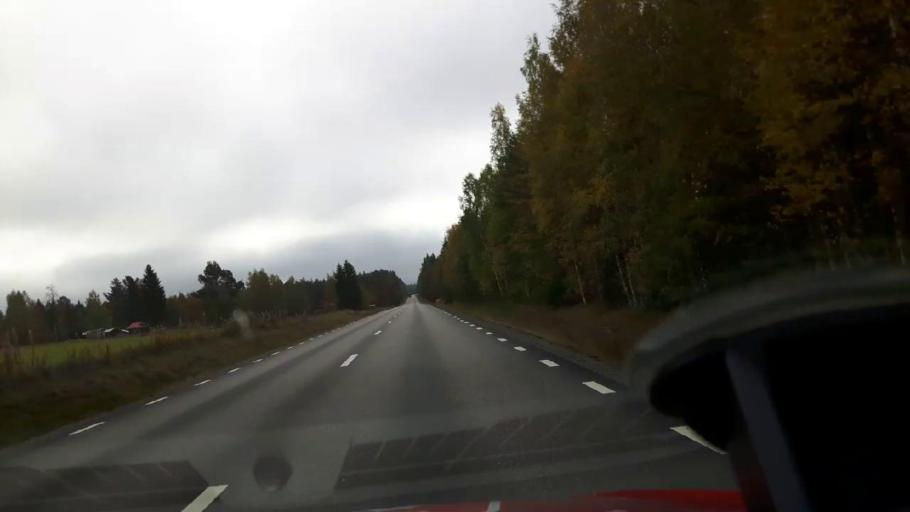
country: SE
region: Gaevleborg
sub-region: Ljusdals Kommun
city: Farila
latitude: 61.8607
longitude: 15.7418
